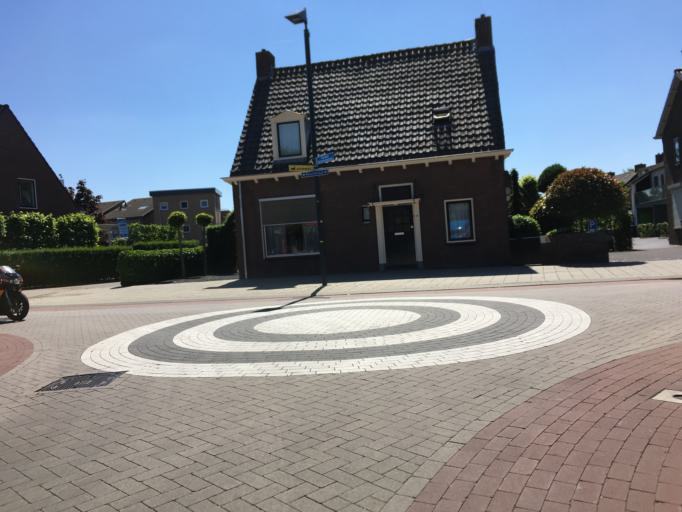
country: NL
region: Gelderland
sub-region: Gemeente Maasdriel
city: Hedel
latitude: 51.7450
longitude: 5.2596
